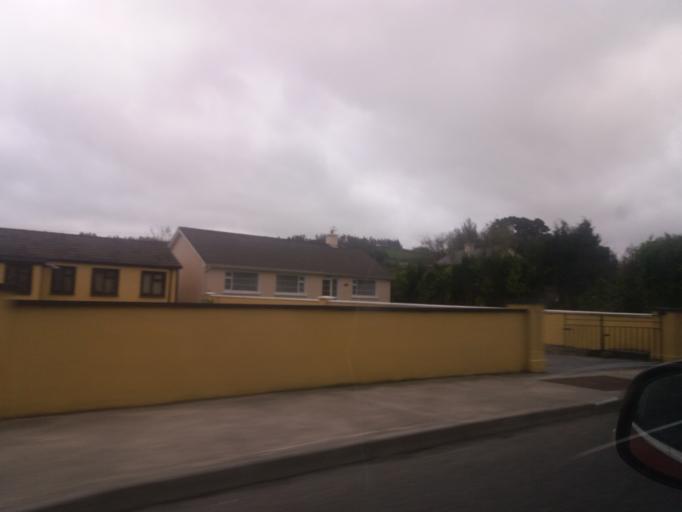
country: IE
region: Munster
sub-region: County Limerick
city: Abbeyfeale
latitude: 52.3813
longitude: -9.3017
